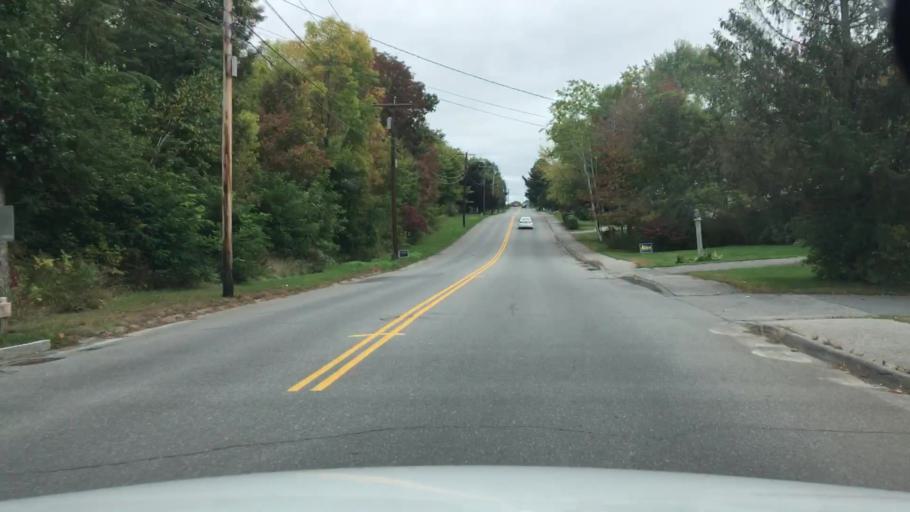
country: US
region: Maine
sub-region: Kennebec County
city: Waterville
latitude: 44.5636
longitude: -69.6444
